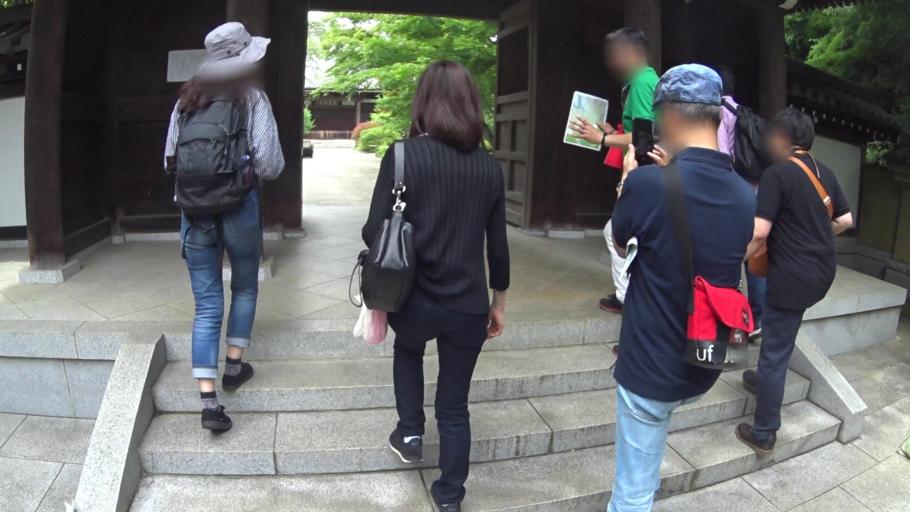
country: JP
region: Tokyo
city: Musashino
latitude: 35.7168
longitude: 139.6074
